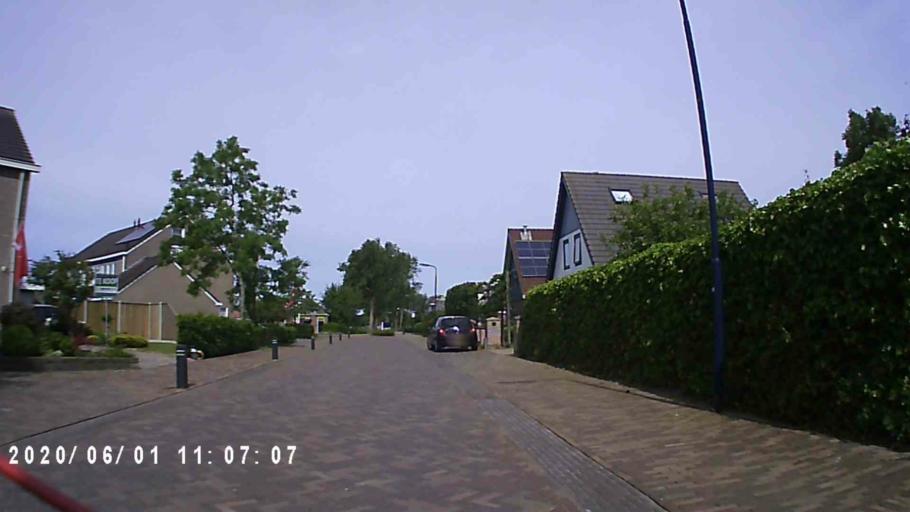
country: NL
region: Friesland
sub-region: Gemeente Franekeradeel
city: Sexbierum
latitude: 53.1967
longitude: 5.4596
